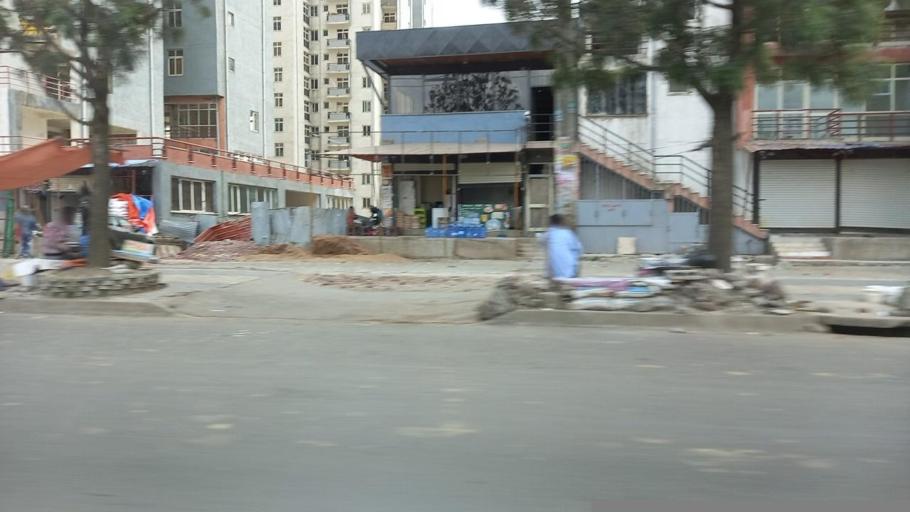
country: ET
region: Adis Abeba
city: Addis Ababa
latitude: 9.0207
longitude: 38.8671
